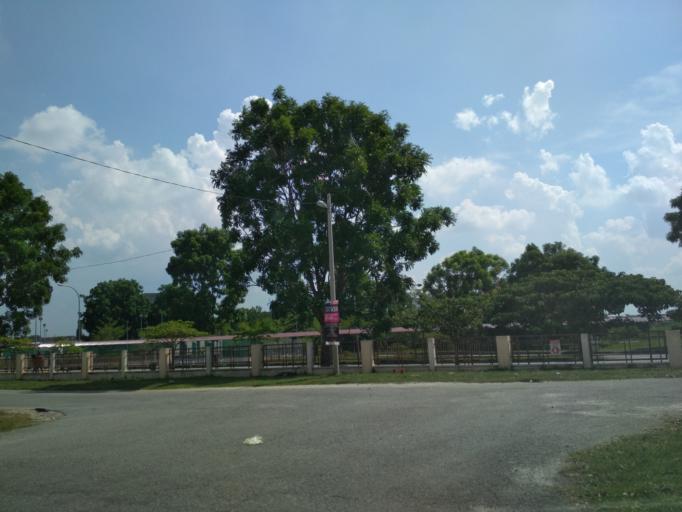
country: MY
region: Perak
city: Kampar
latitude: 4.3305
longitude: 101.1437
